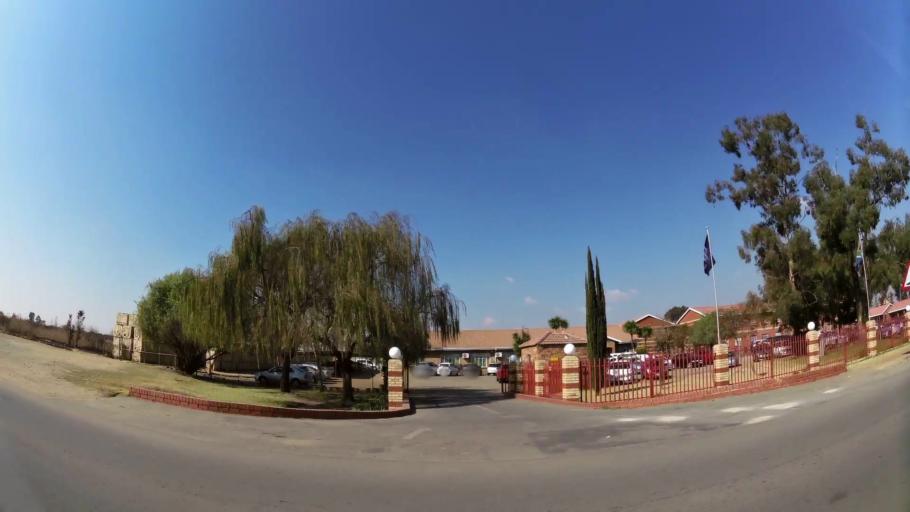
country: ZA
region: Gauteng
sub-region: Ekurhuleni Metropolitan Municipality
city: Benoni
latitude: -26.2063
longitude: 28.3150
